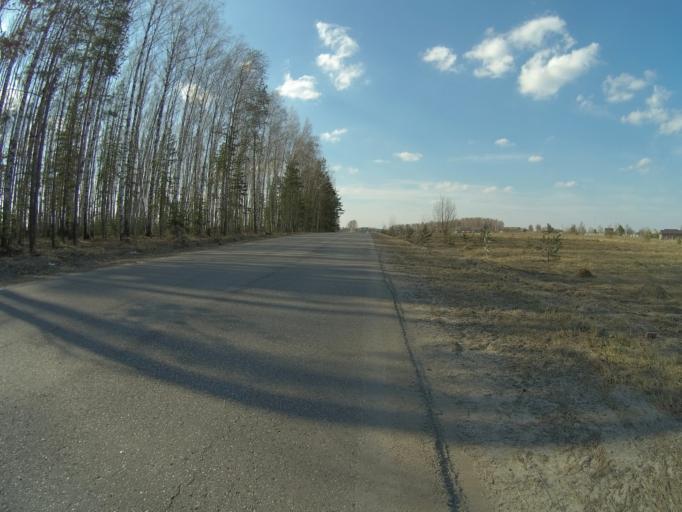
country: RU
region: Vladimir
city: Sudogda
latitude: 56.0651
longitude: 40.8056
